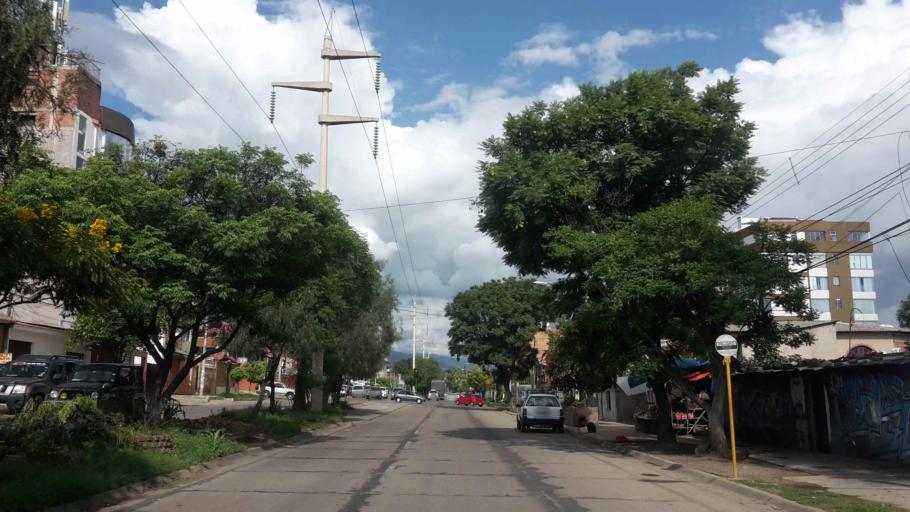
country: BO
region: Cochabamba
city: Cochabamba
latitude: -17.3662
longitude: -66.1553
